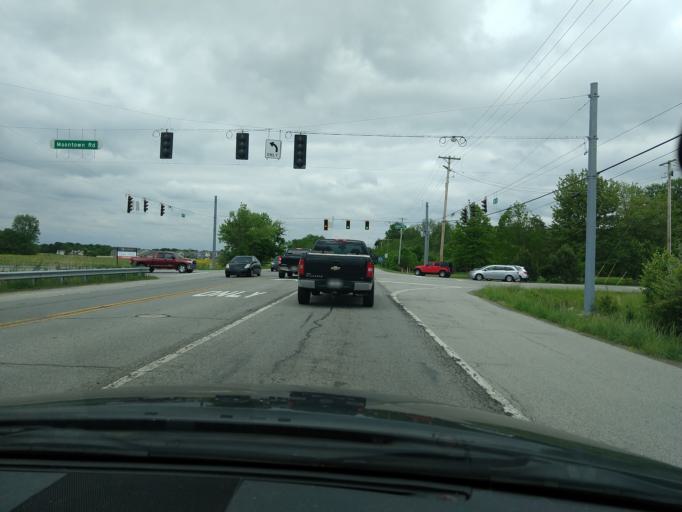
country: US
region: Indiana
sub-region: Hamilton County
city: Westfield
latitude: 40.0430
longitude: -86.0905
